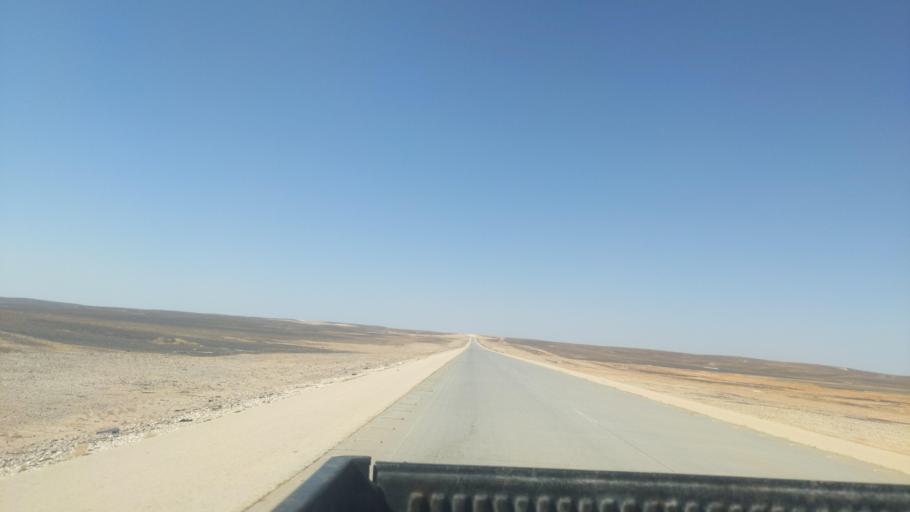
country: JO
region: Amman
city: Al Azraq ash Shamali
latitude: 31.4105
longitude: 36.7179
